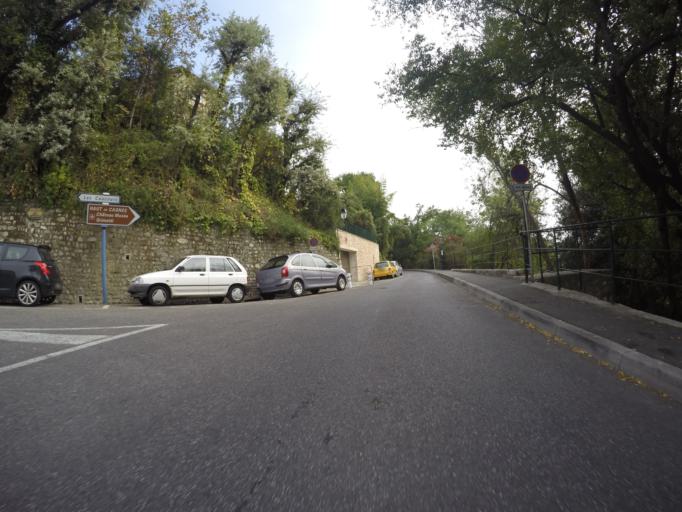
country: FR
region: Provence-Alpes-Cote d'Azur
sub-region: Departement des Alpes-Maritimes
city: Cagnes-sur-Mer
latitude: 43.6696
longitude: 7.1453
